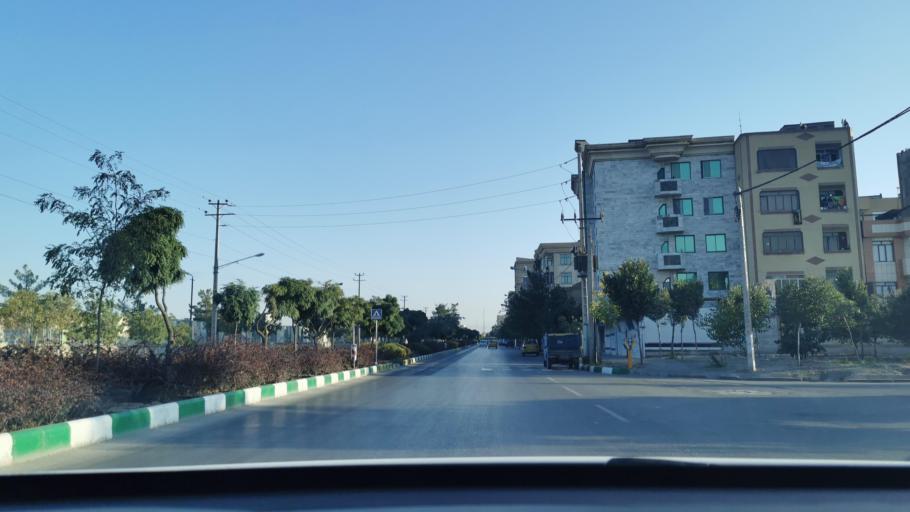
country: IR
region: Razavi Khorasan
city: Mashhad
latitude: 36.3477
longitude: 59.5141
